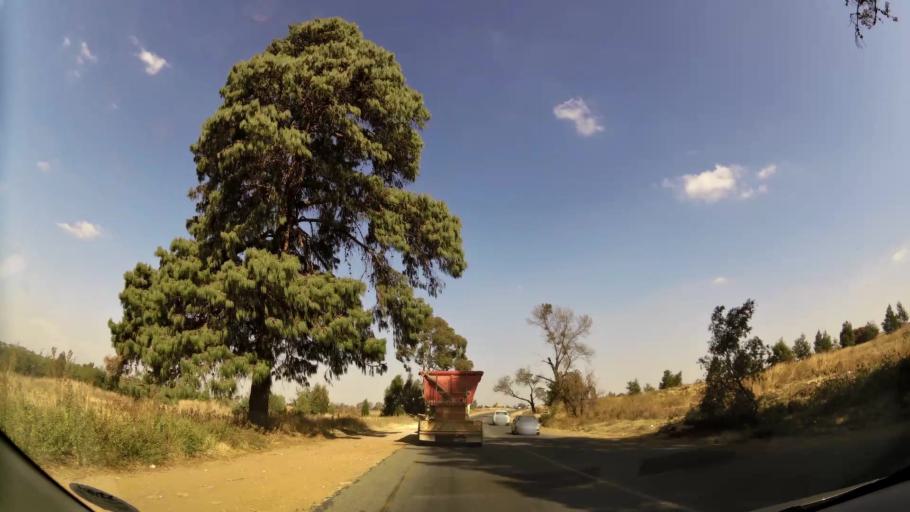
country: ZA
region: Gauteng
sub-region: West Rand District Municipality
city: Krugersdorp
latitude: -26.1276
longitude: 27.8144
